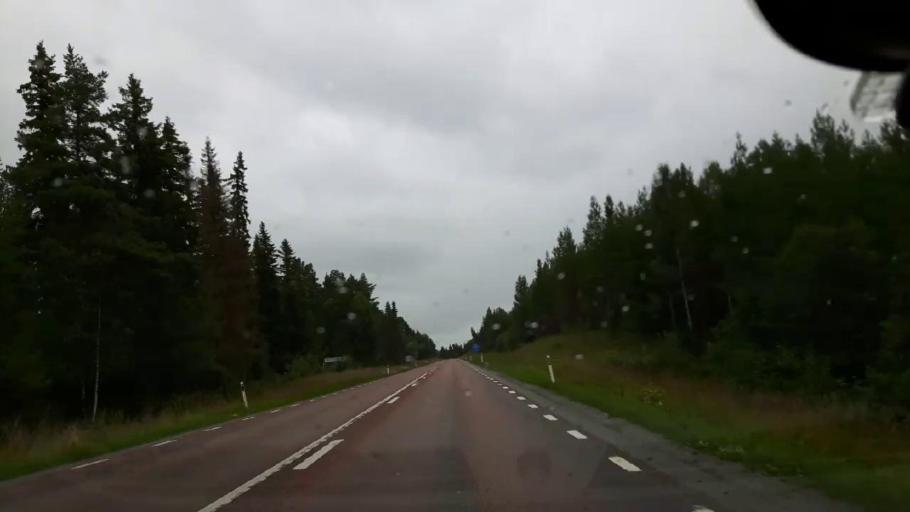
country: SE
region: Jaemtland
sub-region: Bergs Kommun
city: Hoverberg
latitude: 62.9523
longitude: 14.5467
